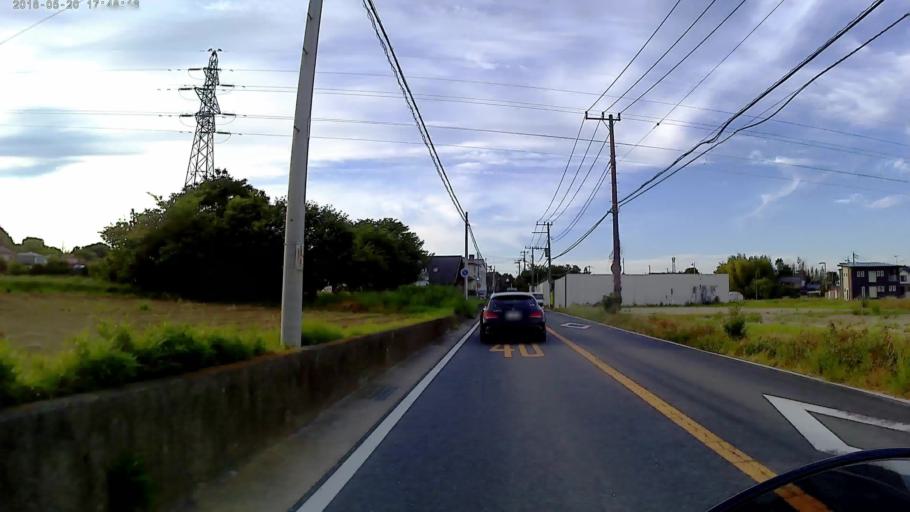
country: JP
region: Kanagawa
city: Oiso
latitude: 35.3389
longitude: 139.2927
